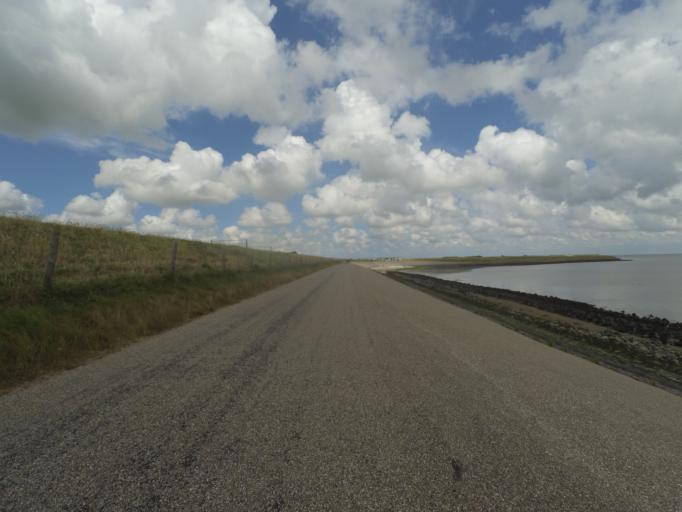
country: NL
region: North Holland
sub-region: Gemeente Texel
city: Den Burg
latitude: 53.0632
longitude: 4.8725
